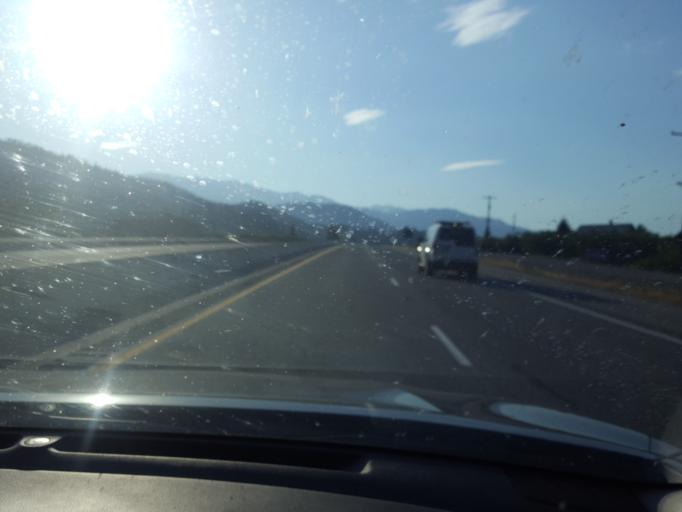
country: US
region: Washington
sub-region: Chelan County
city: Cashmere
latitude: 47.5362
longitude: -120.5534
